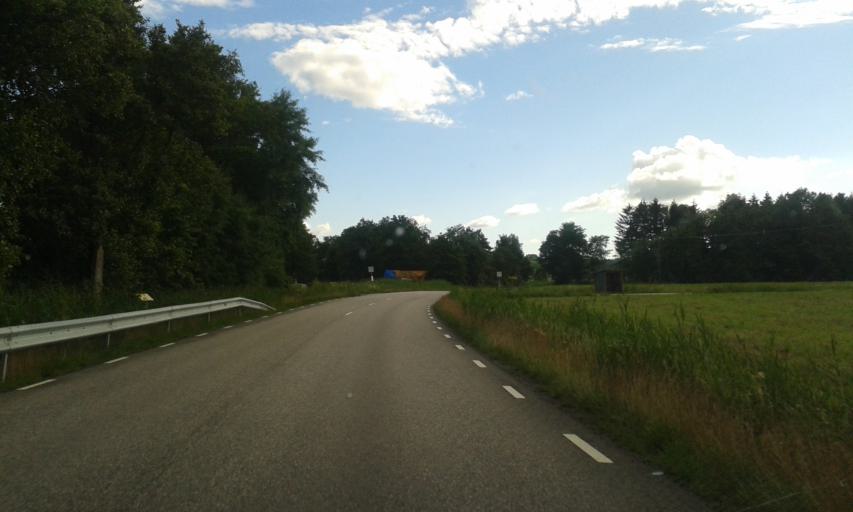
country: SE
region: Vaestra Goetaland
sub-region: Ale Kommun
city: Alafors
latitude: 57.9488
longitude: 12.0701
